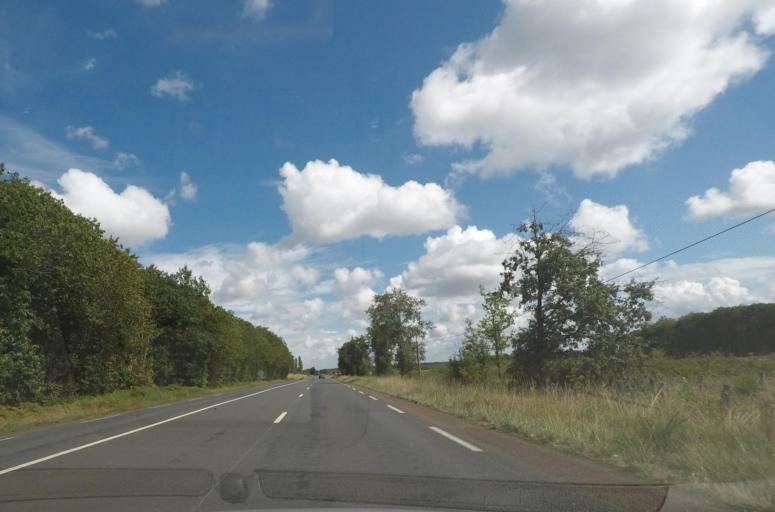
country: FR
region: Pays de la Loire
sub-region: Departement de la Sarthe
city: Clermont-Creans
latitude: 47.7671
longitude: 0.0204
